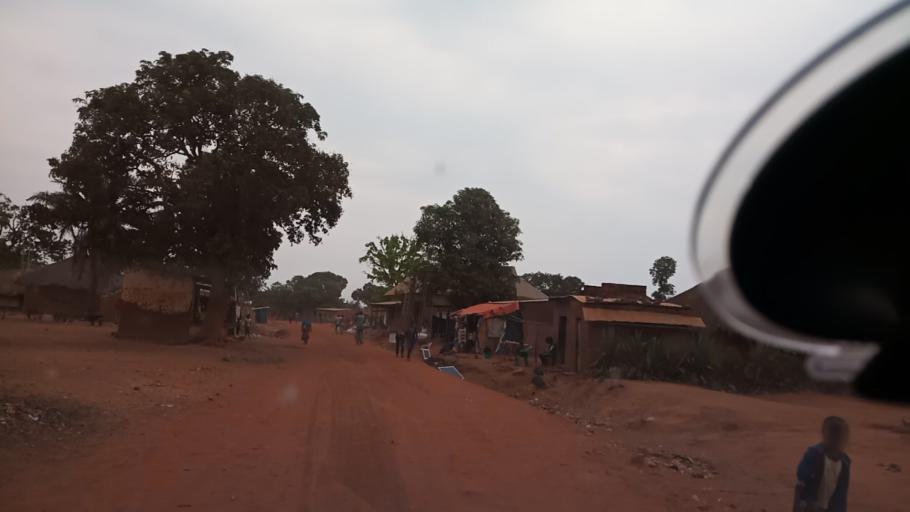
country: ZM
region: Luapula
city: Nchelenge
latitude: -9.2773
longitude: 28.3326
